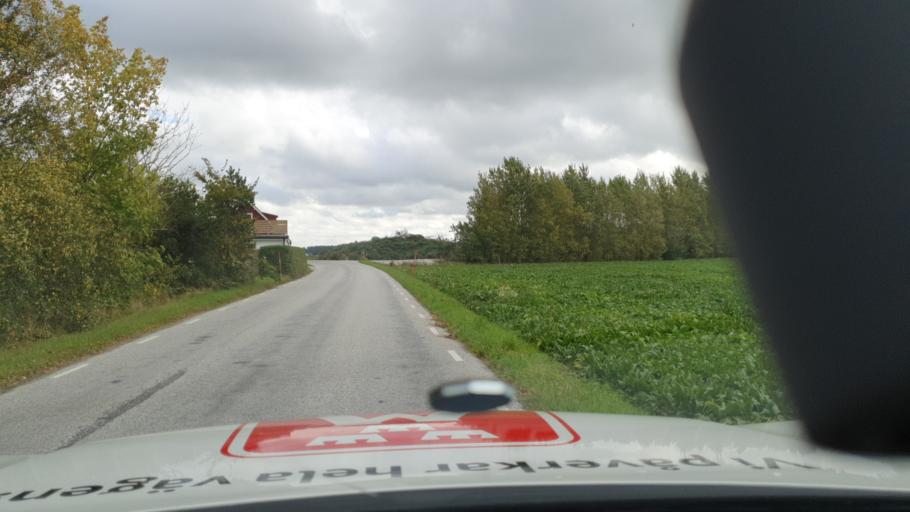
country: SE
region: Skane
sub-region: Malmo
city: Oxie
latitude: 55.5110
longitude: 13.1162
